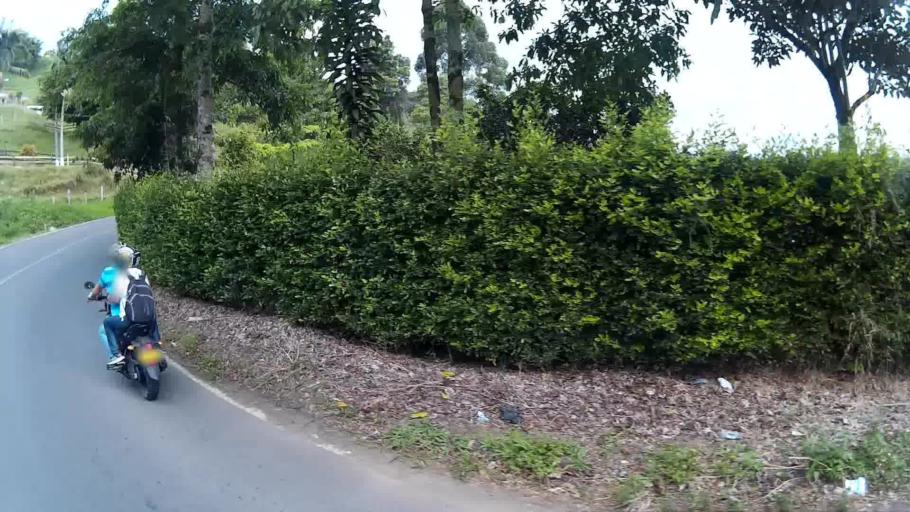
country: CO
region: Risaralda
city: Marsella
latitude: 4.8946
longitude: -75.7462
